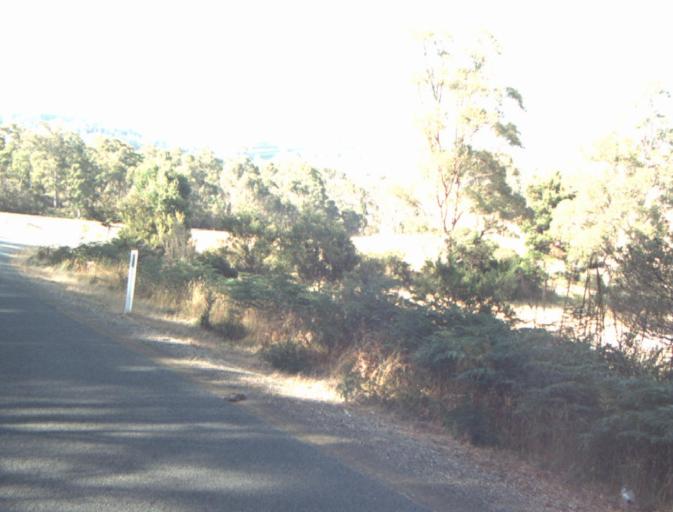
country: AU
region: Tasmania
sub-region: Dorset
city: Bridport
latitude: -41.1479
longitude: 147.2331
